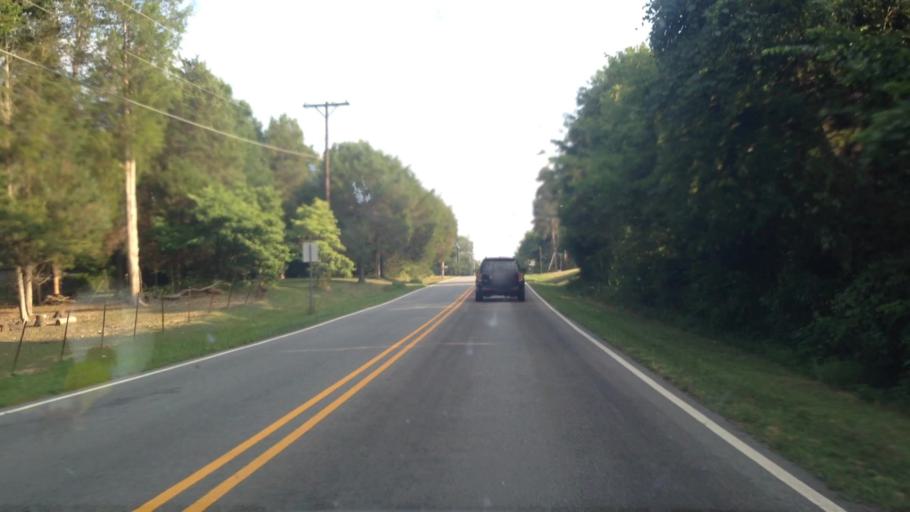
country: US
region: North Carolina
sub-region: Guilford County
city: High Point
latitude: 36.0106
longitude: -80.0606
